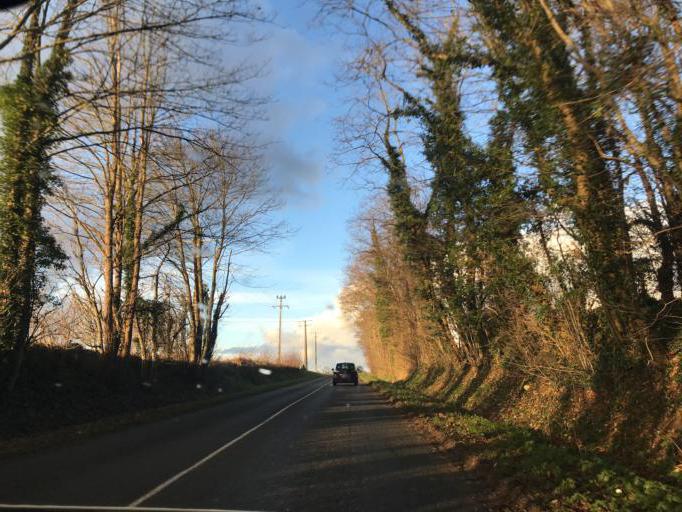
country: FR
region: Ile-de-France
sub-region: Departement de Seine-et-Marne
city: Juilly
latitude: 49.0034
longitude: 2.7009
